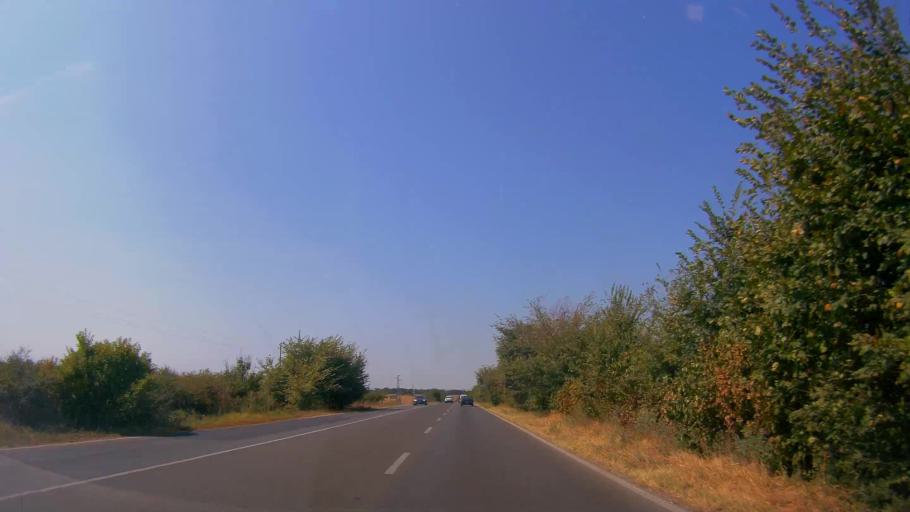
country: BG
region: Ruse
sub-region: Obshtina Vetovo
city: Senovo
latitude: 43.5647
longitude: 26.3371
